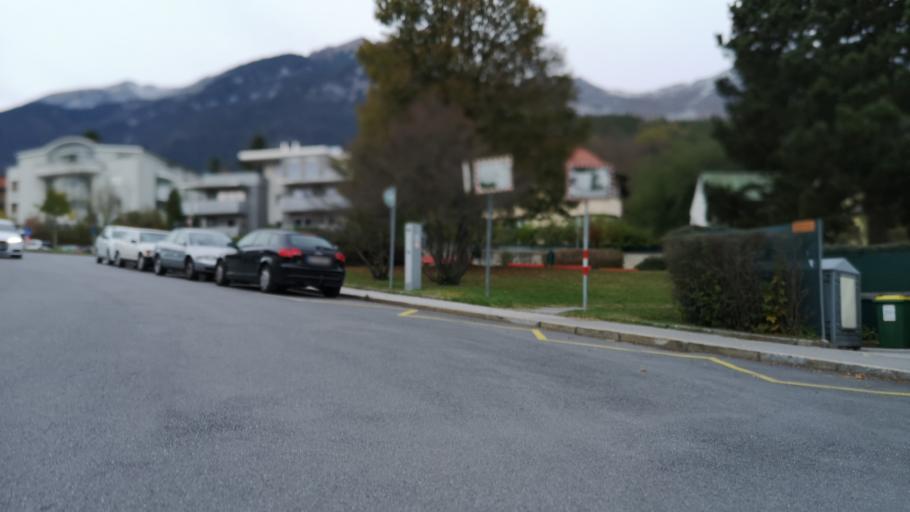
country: AT
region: Tyrol
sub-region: Innsbruck Stadt
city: Innsbruck
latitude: 47.2679
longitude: 11.3730
